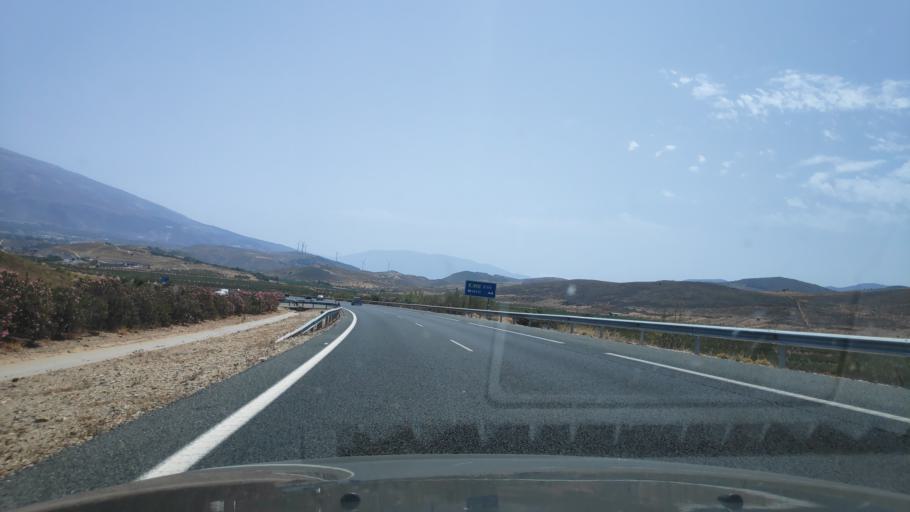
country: ES
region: Andalusia
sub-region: Provincia de Granada
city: Padul
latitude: 36.9928
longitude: -3.6268
